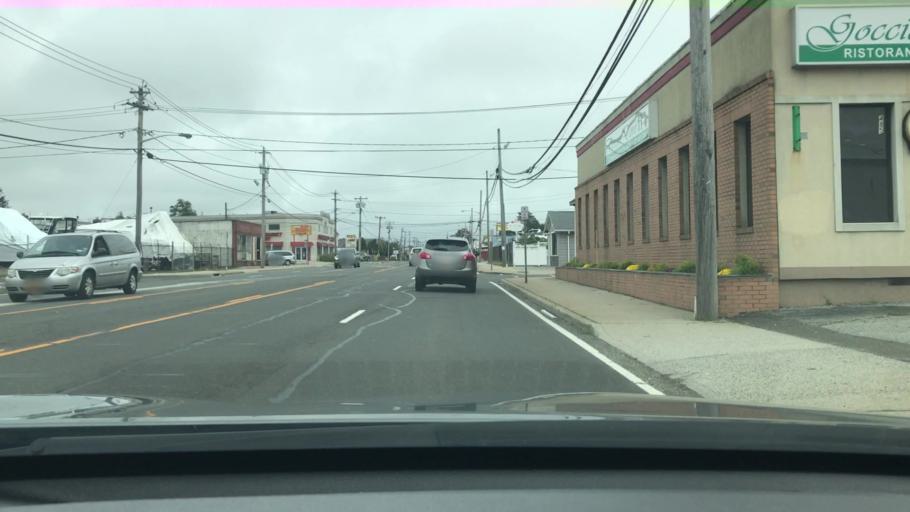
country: US
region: New York
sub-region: Suffolk County
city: Lindenhurst
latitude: 40.6734
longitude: -73.3751
